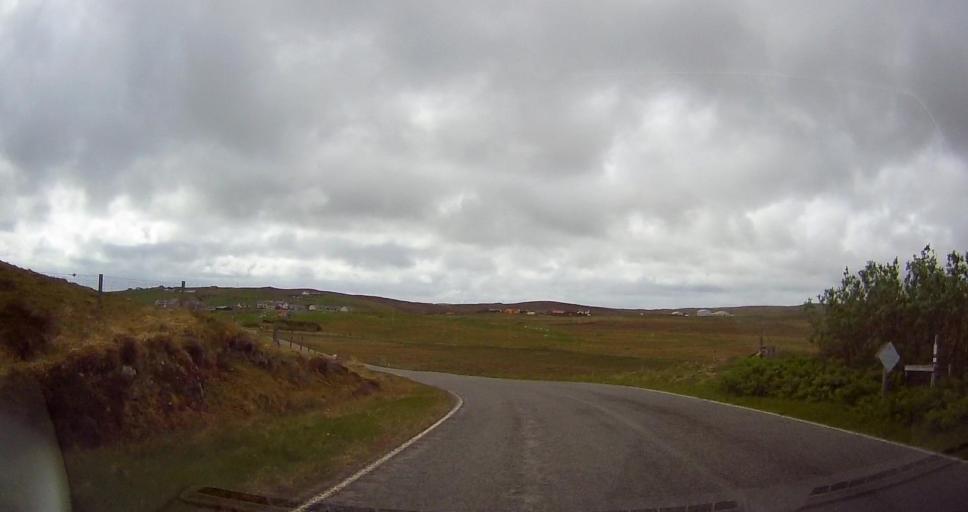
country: GB
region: Scotland
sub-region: Shetland Islands
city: Sandwick
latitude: 60.2328
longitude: -1.5539
